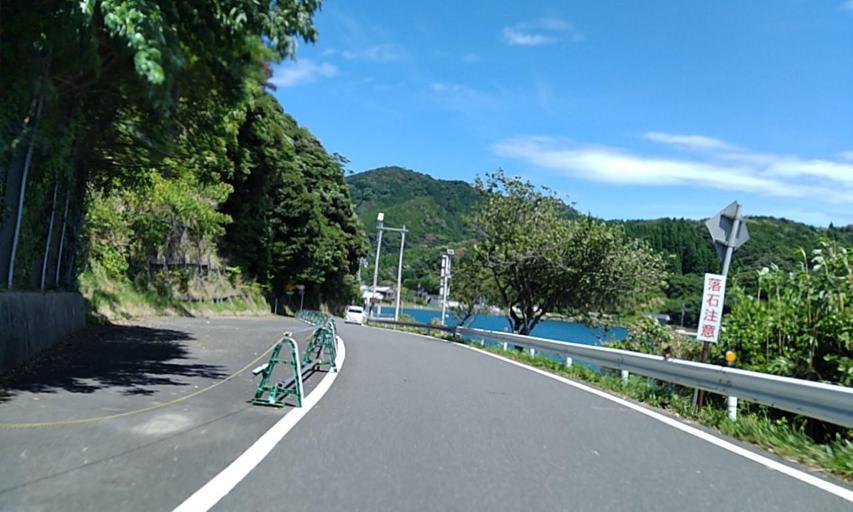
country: JP
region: Kyoto
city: Miyazu
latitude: 35.6689
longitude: 135.2755
